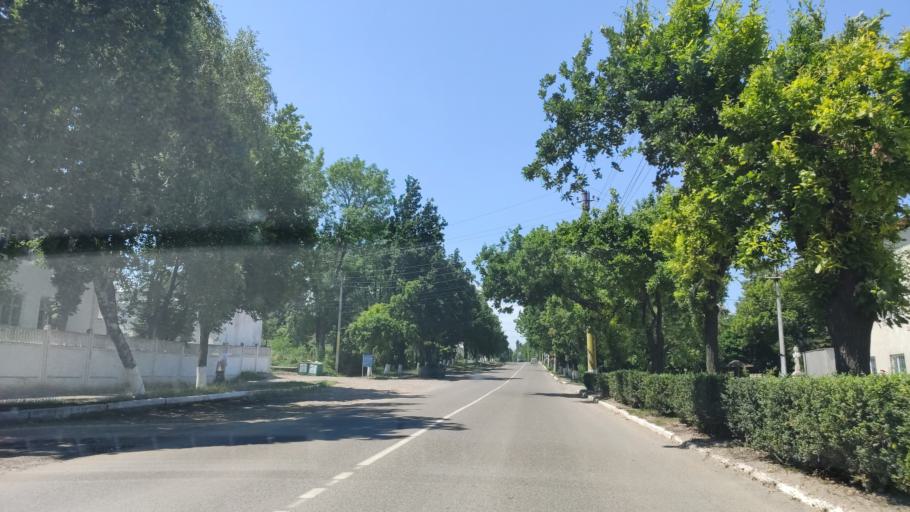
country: MD
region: Raionul Soroca
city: Soroca
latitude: 48.1620
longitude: 28.2860
